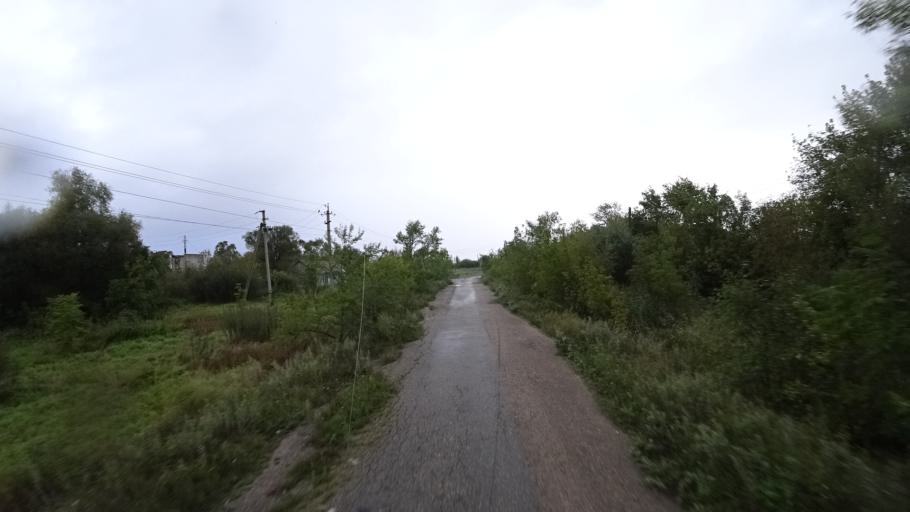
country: RU
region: Primorskiy
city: Chernigovka
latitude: 44.4041
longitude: 132.5316
